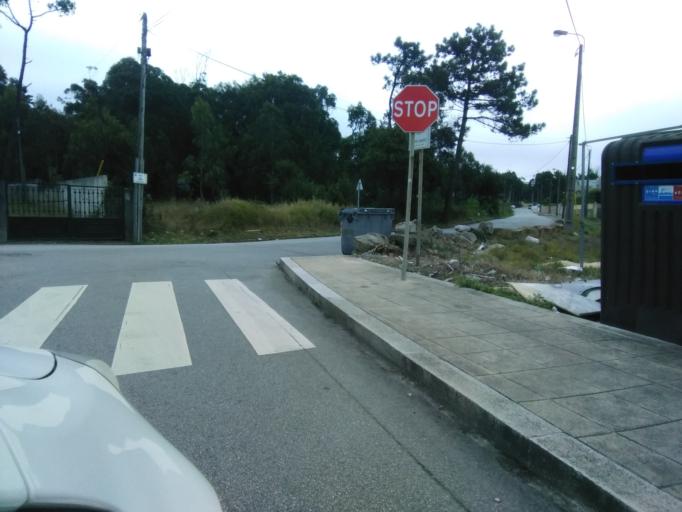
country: PT
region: Porto
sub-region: Matosinhos
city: Lavra
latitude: 41.2480
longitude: -8.7183
